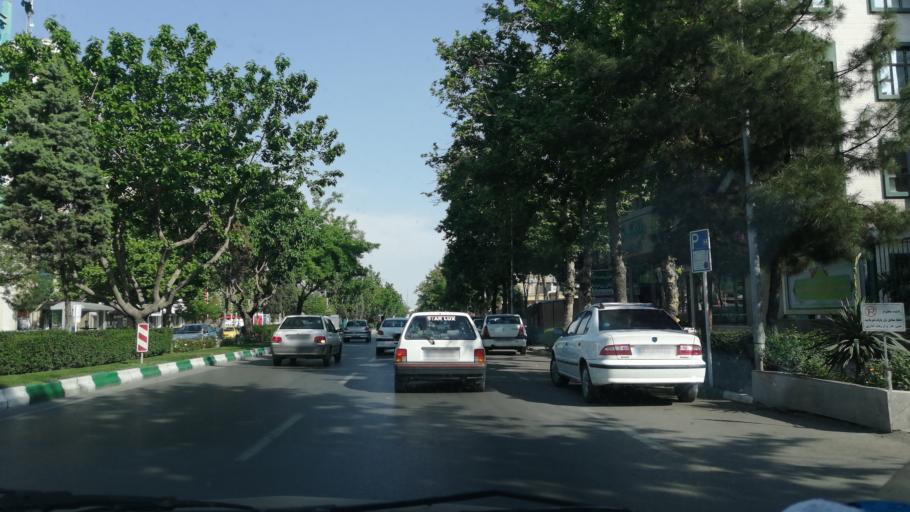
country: IR
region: Razavi Khorasan
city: Mashhad
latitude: 36.3138
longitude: 59.5616
